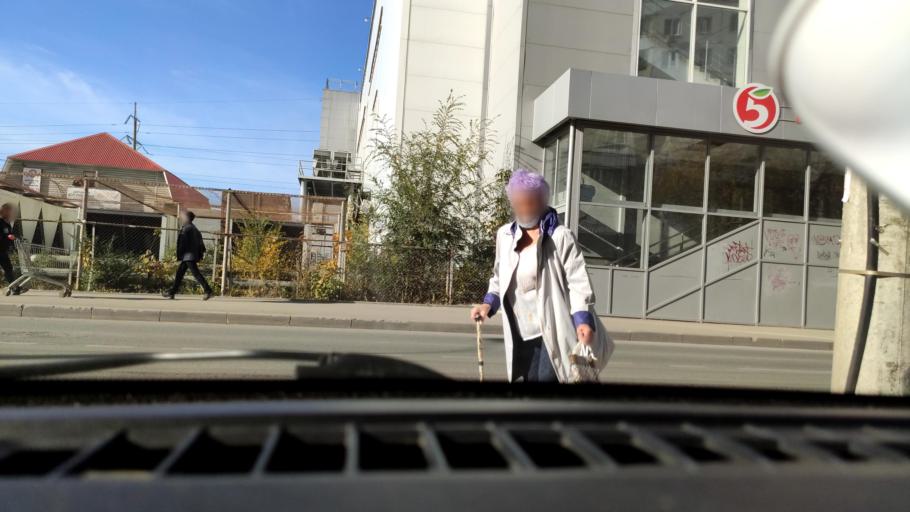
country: RU
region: Samara
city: Samara
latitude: 53.2478
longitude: 50.2205
